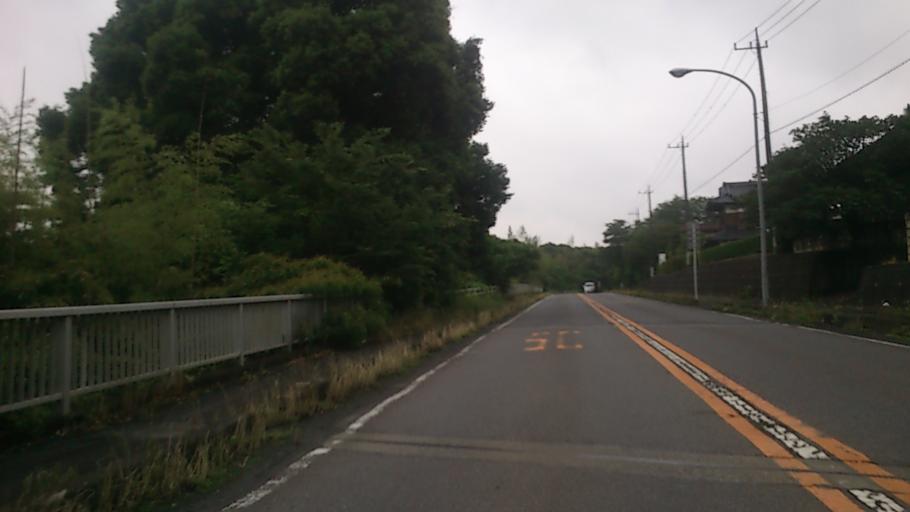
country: JP
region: Ibaraki
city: Omiya
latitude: 36.6219
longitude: 140.4031
